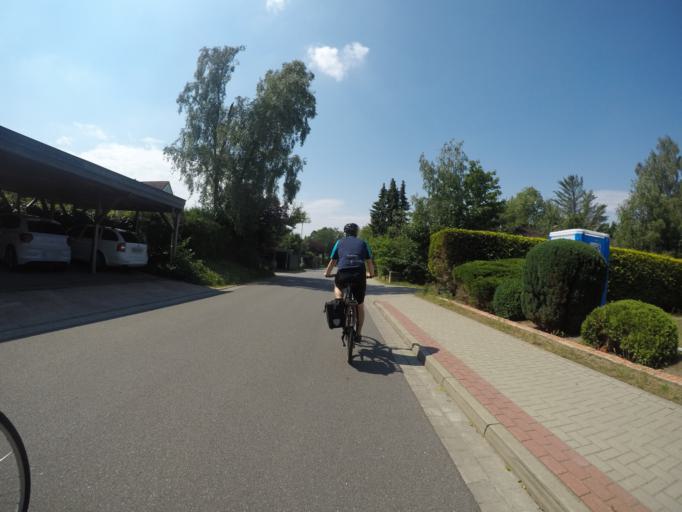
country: DE
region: Lower Saxony
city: Buchholz in der Nordheide
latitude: 53.3292
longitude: 9.8465
